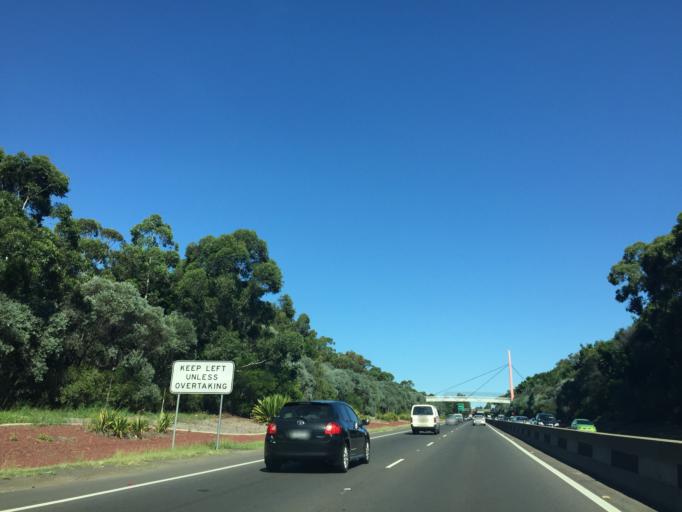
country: AU
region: New South Wales
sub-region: Strathfield
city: Homebush
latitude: -33.8598
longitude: 151.0772
